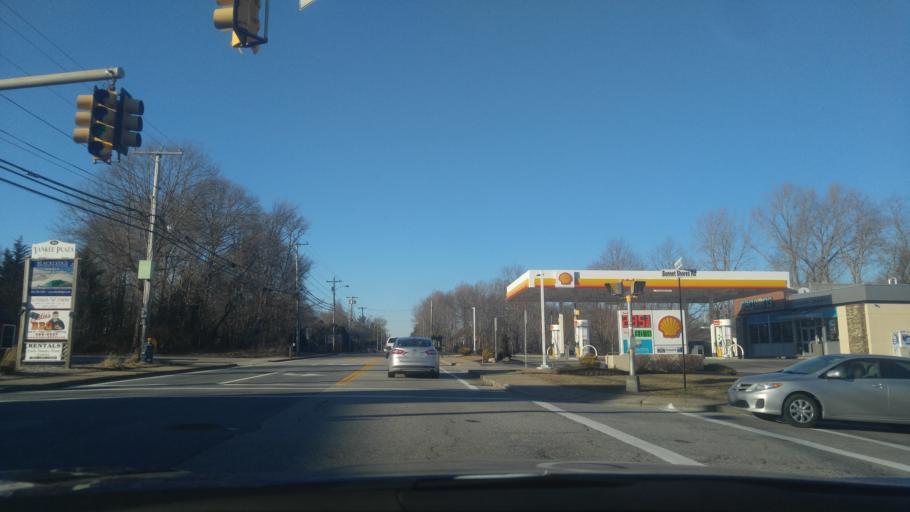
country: US
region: Rhode Island
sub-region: Washington County
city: Narragansett Pier
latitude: 41.4813
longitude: -71.4366
